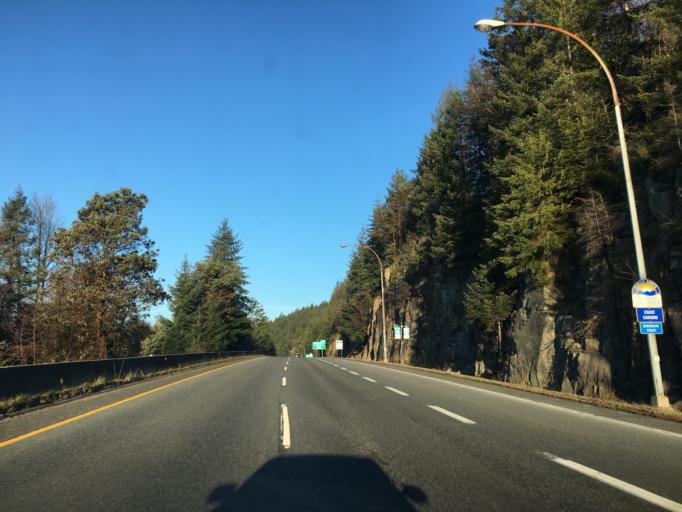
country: CA
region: British Columbia
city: West Vancouver
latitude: 49.3471
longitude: -123.2223
